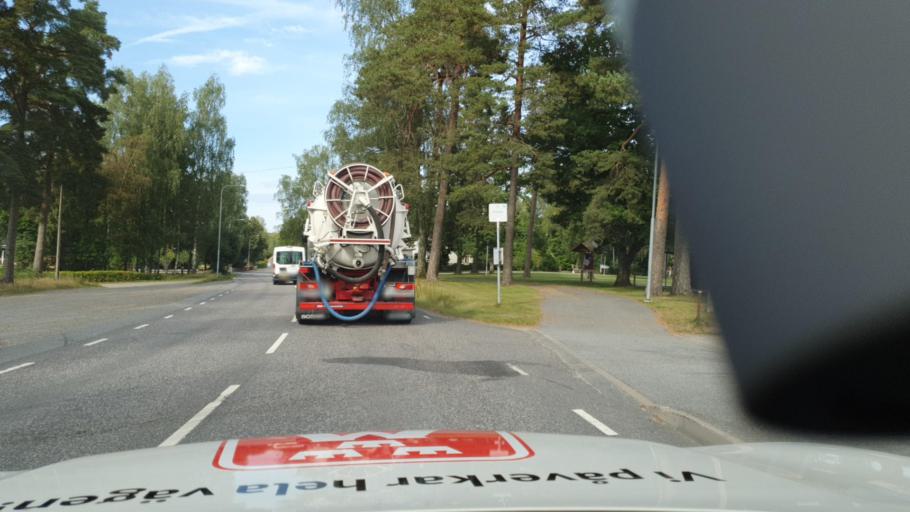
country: SE
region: Vaestra Goetaland
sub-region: Marks Kommun
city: Kinna
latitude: 57.4756
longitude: 12.7053
